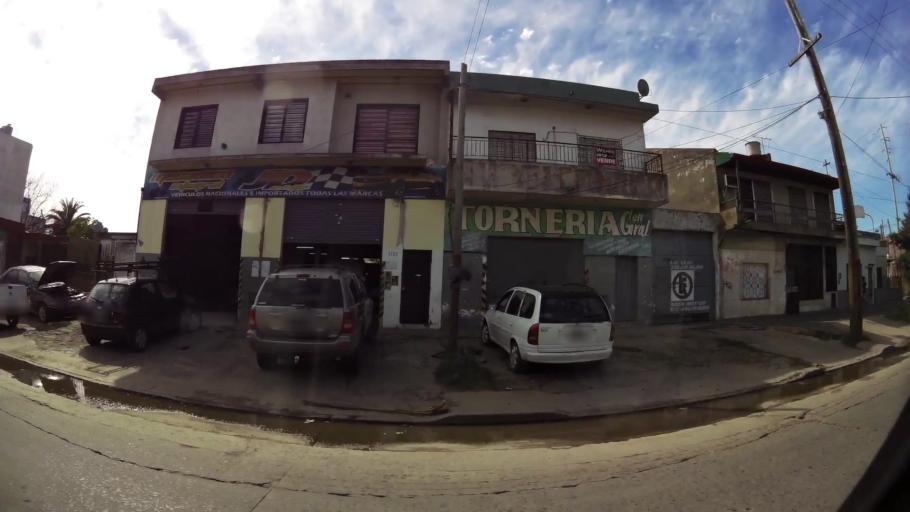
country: AR
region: Buenos Aires
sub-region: Partido de Quilmes
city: Quilmes
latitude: -34.7736
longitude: -58.3012
